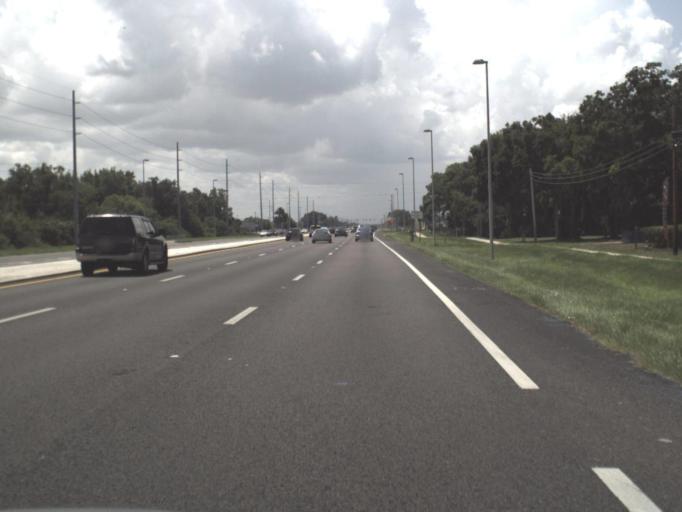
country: US
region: Florida
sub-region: Hillsborough County
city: Riverview
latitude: 27.8279
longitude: -82.3301
